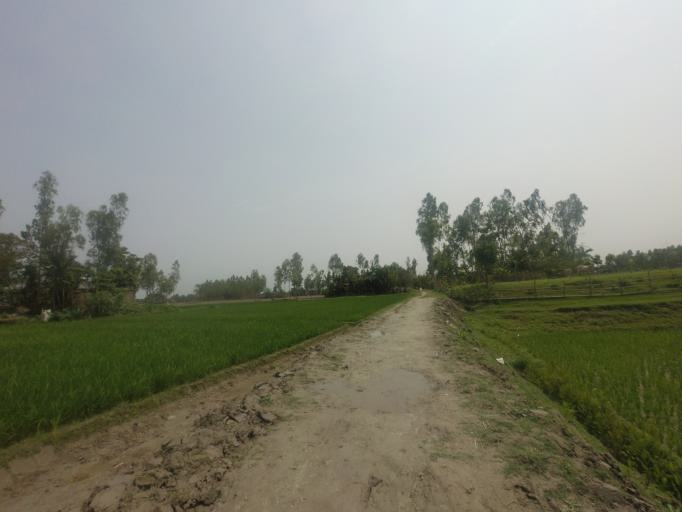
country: BD
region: Rajshahi
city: Sirajganj
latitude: 24.3577
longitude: 89.7210
